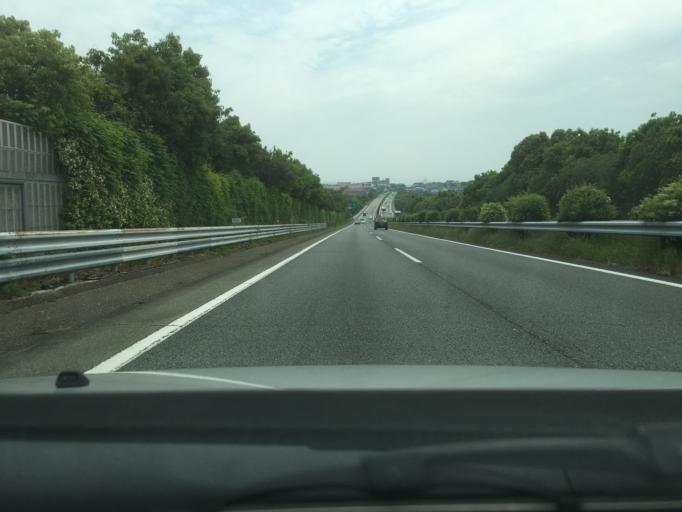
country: JP
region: Kumamoto
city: Kumamoto
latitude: 32.8464
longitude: 130.7700
